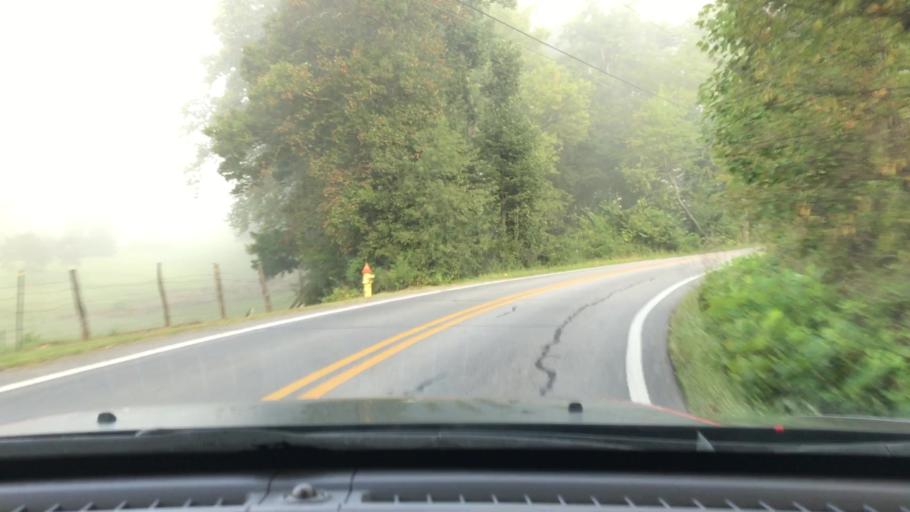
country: US
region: North Carolina
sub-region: Buncombe County
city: Woodfin
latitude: 35.6250
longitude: -82.6128
